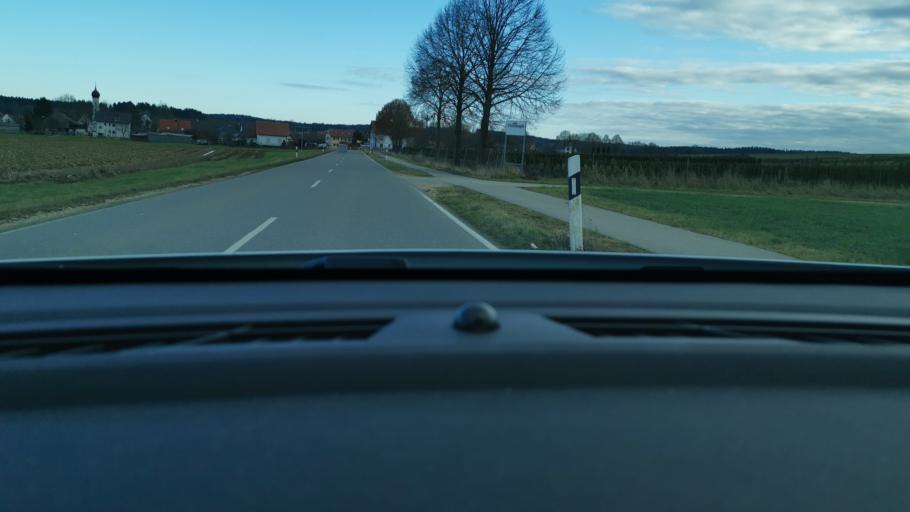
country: DE
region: Bavaria
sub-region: Swabia
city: Affing
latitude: 48.4990
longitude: 10.9932
